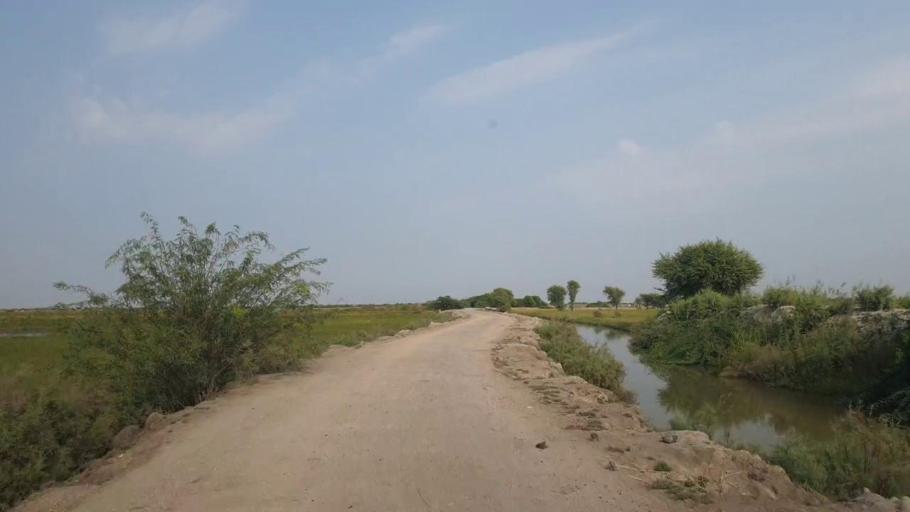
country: PK
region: Sindh
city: Kadhan
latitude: 24.4596
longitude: 68.8101
